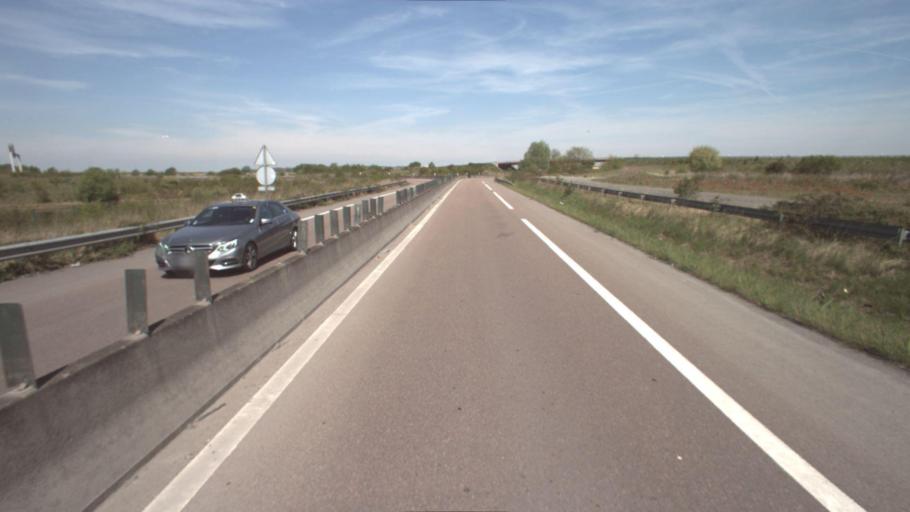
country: FR
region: Ile-de-France
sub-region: Departement de Seine-et-Marne
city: Mitry-Mory
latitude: 49.0002
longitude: 2.6409
